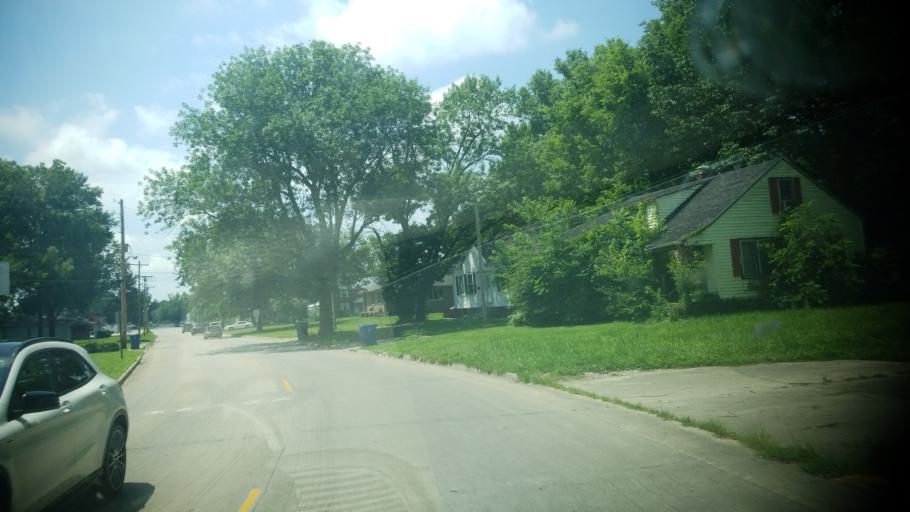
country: US
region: Illinois
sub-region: Wayne County
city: Fairfield
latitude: 38.3816
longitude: -88.3538
